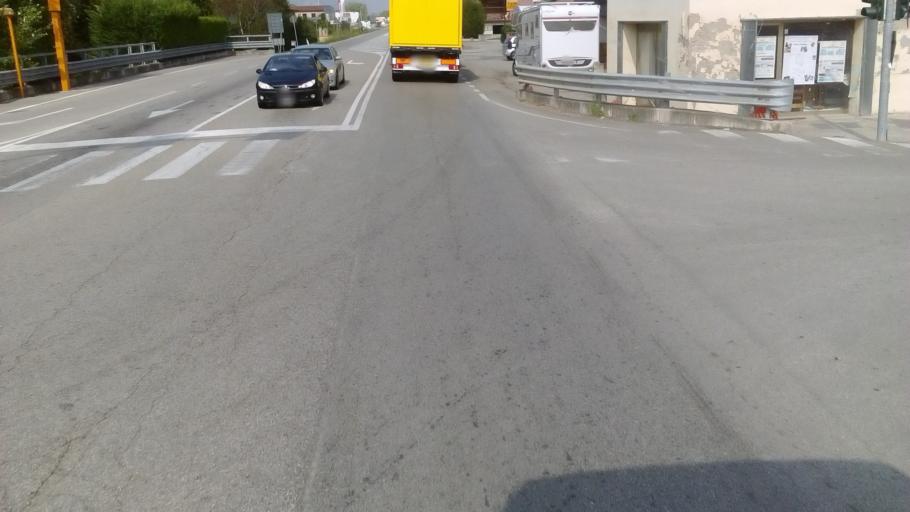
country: IT
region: Veneto
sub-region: Provincia di Padova
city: Solesino
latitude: 45.1821
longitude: 11.7561
